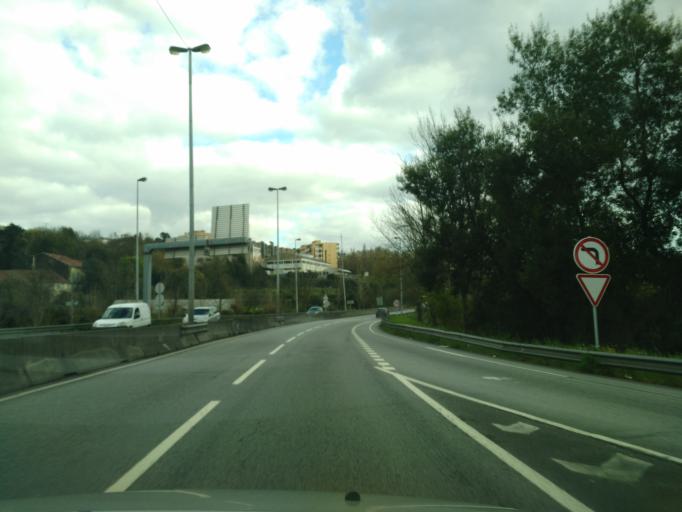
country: PT
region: Braga
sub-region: Guimaraes
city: Guimaraes
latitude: 41.4388
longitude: -8.3059
